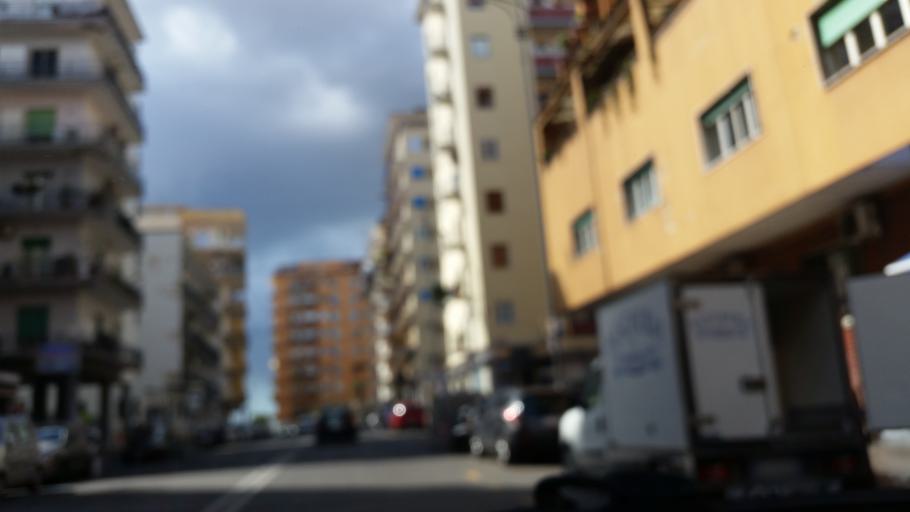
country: IT
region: Campania
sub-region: Provincia di Napoli
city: Napoli
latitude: 40.8431
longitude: 14.2212
